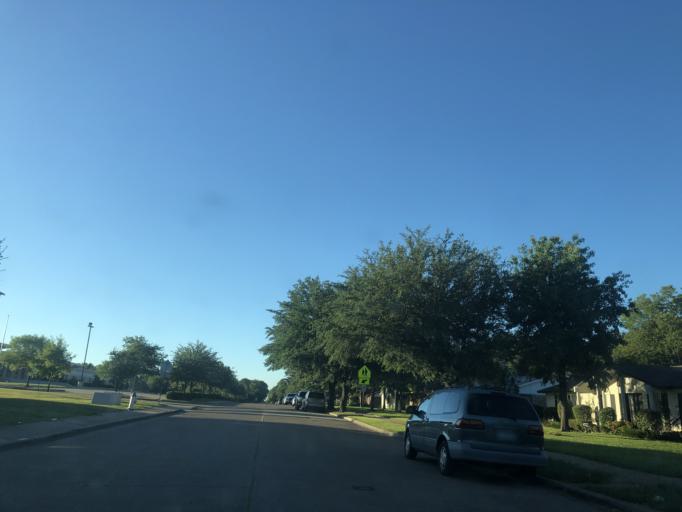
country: US
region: Texas
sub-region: Dallas County
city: Garland
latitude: 32.8356
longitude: -96.6419
